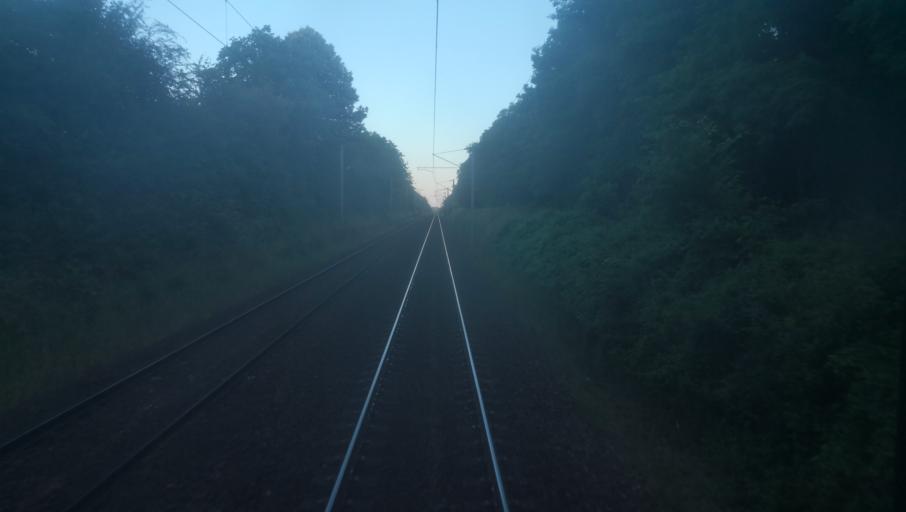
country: FR
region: Bourgogne
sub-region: Departement de la Nievre
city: La Charite-sur-Loire
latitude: 47.2209
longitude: 3.0170
